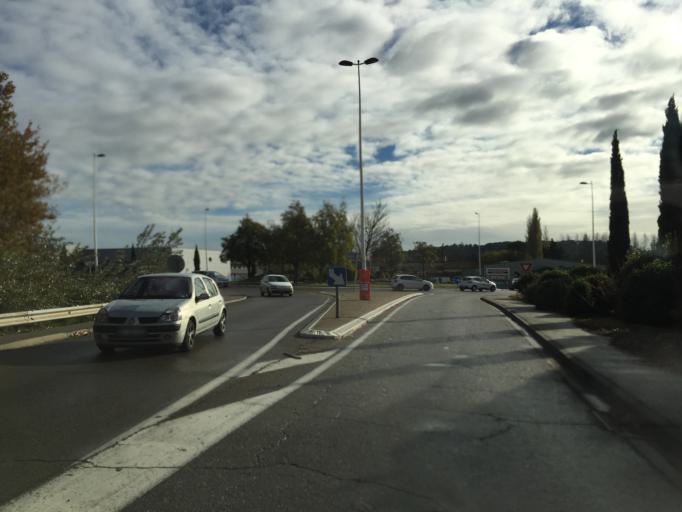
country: FR
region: Provence-Alpes-Cote d'Azur
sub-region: Departement du Vaucluse
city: Vedene
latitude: 43.9904
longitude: 4.8915
